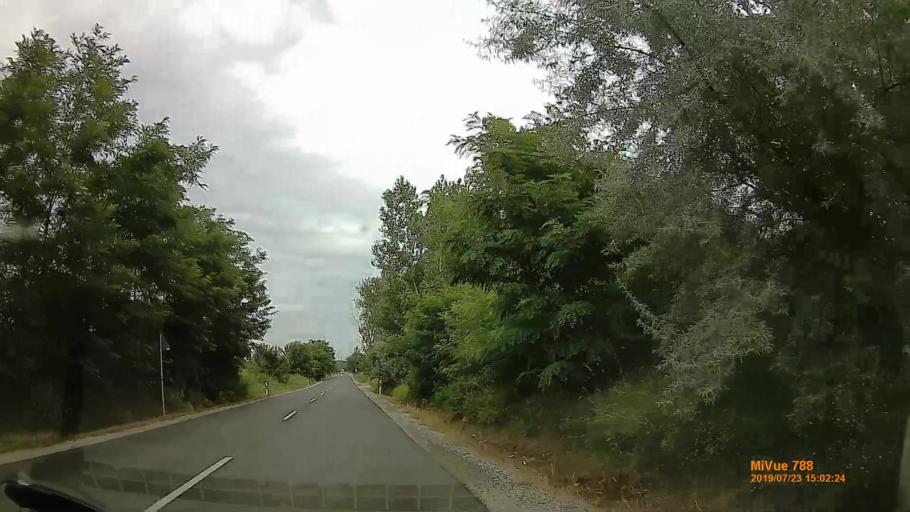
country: HU
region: Szabolcs-Szatmar-Bereg
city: Nyiregyhaza
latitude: 47.9317
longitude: 21.6979
